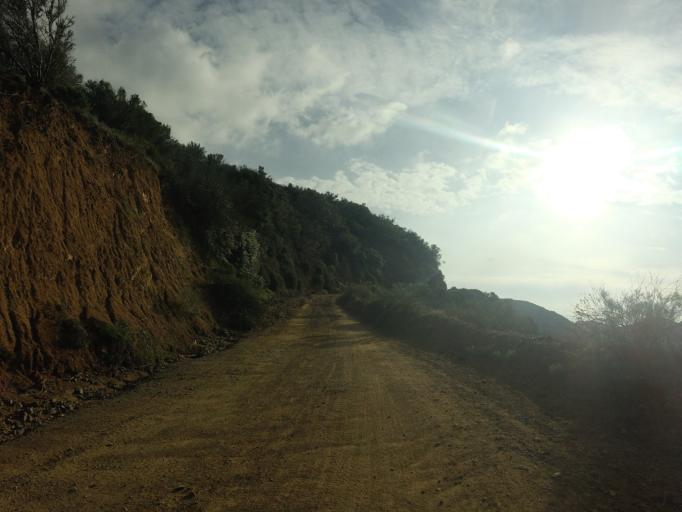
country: US
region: California
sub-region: Riverside County
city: Corona
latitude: 33.8391
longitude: -117.6268
